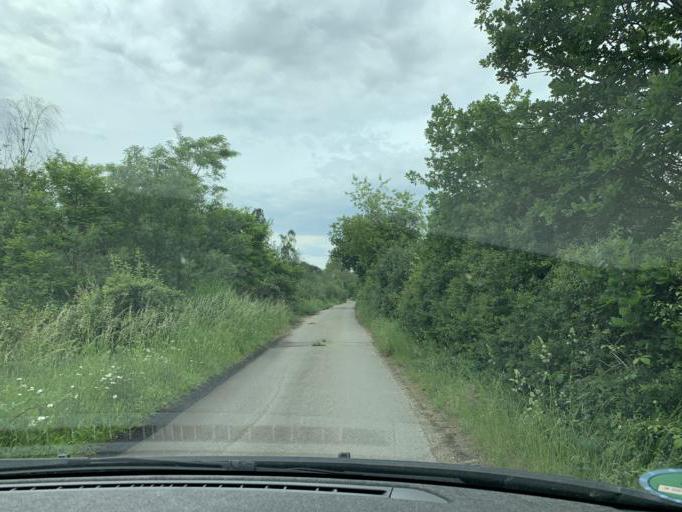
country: DE
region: North Rhine-Westphalia
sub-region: Regierungsbezirk Koln
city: Niederzier
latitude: 50.8769
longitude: 6.5087
